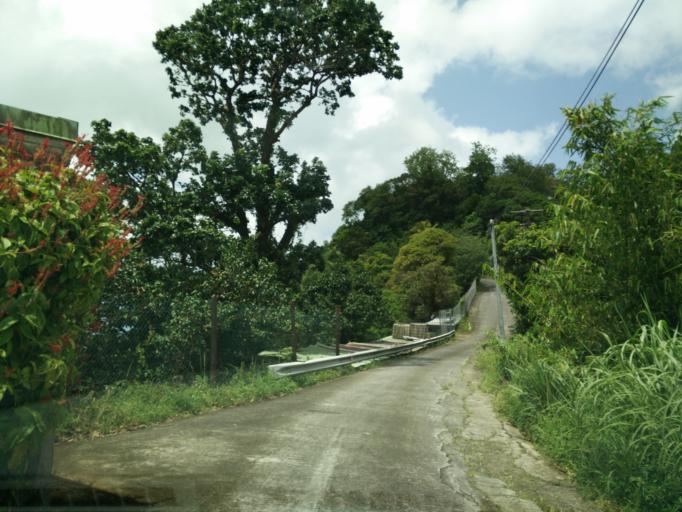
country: MQ
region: Martinique
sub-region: Martinique
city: Le Morne-Rouge
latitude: 14.7385
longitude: -61.1379
